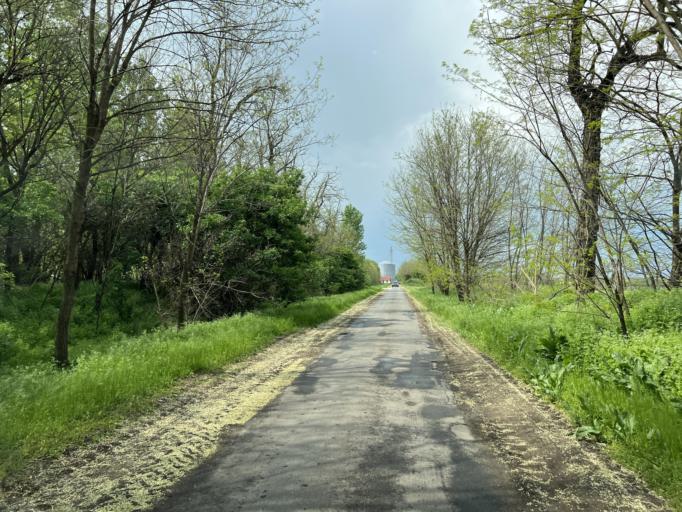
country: HU
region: Pest
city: Nagykoros
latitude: 46.9794
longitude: 19.8099
